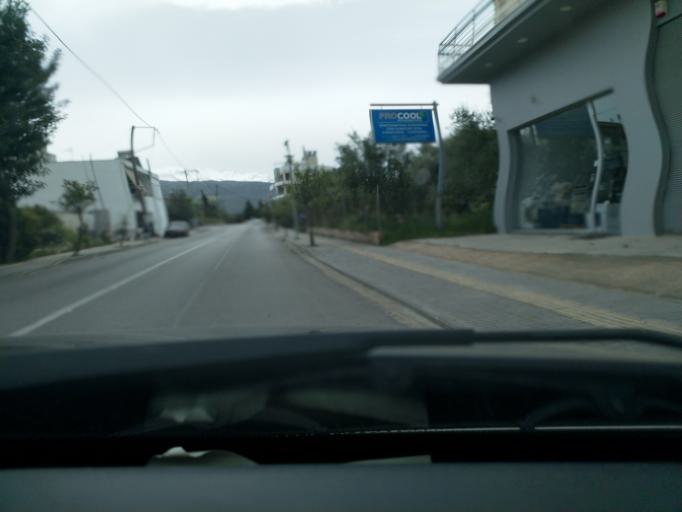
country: GR
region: Crete
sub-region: Nomos Chanias
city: Chania
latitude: 35.5003
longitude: 24.0216
